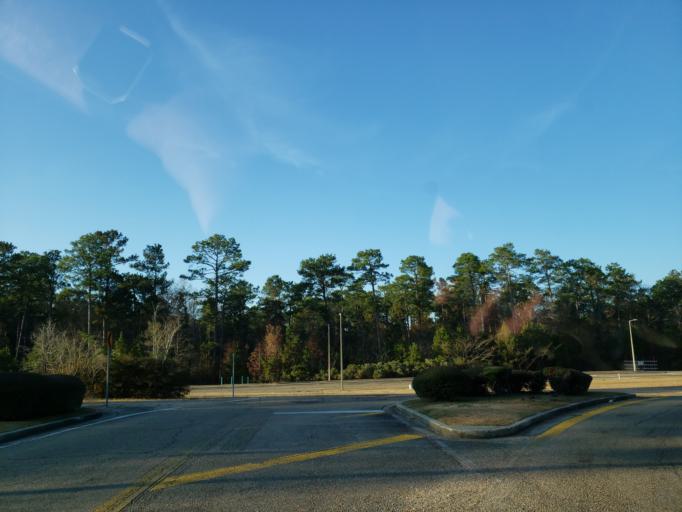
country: US
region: Mississippi
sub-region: Lamar County
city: Arnold Line
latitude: 31.3540
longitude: -89.3614
